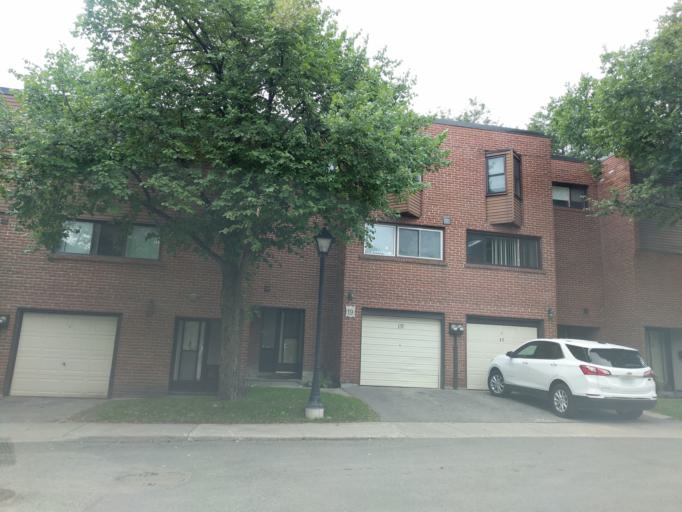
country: CA
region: Ontario
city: Willowdale
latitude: 43.8112
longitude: -79.3552
